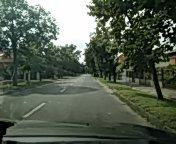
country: HU
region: Hajdu-Bihar
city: Debrecen
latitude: 47.5335
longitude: 21.6579
